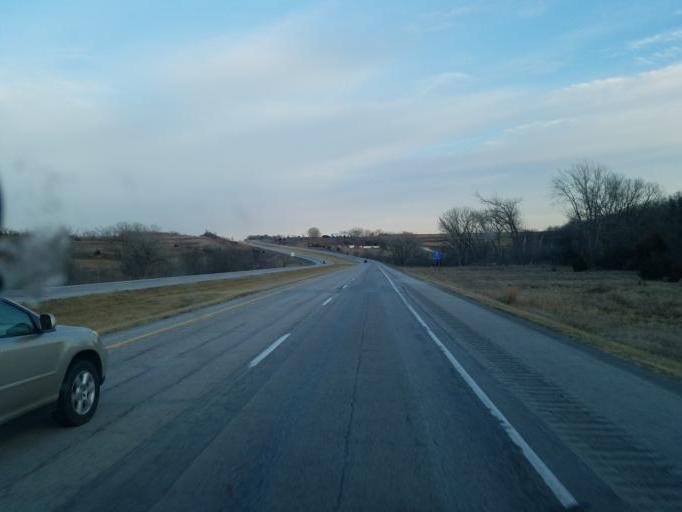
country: US
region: Iowa
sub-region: Harrison County
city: Missouri Valley
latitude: 41.4940
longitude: -95.8592
